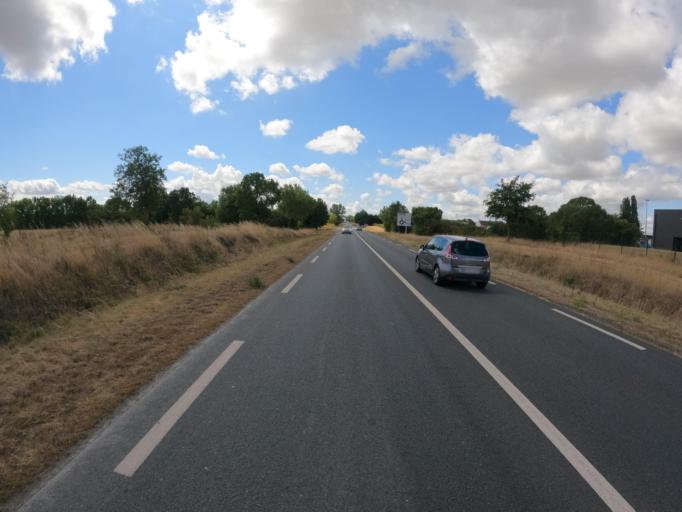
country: FR
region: Pays de la Loire
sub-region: Departement de la Loire-Atlantique
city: Ancenis
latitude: 47.3859
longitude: -1.1726
